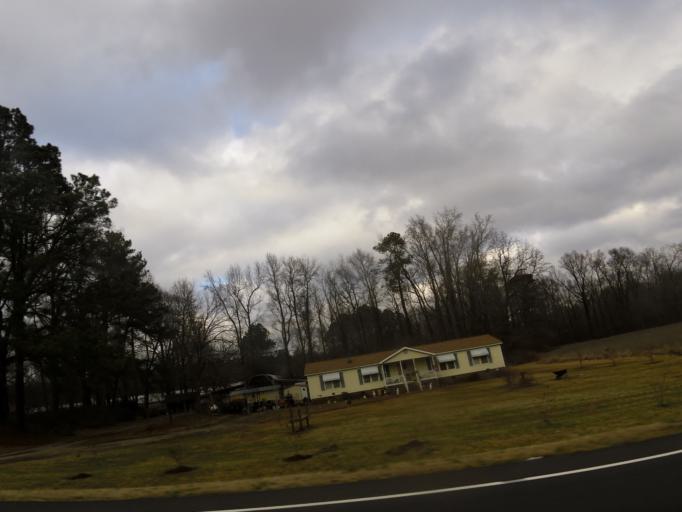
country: US
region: North Carolina
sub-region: Nash County
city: Rocky Mount
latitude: 35.8717
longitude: -77.7387
